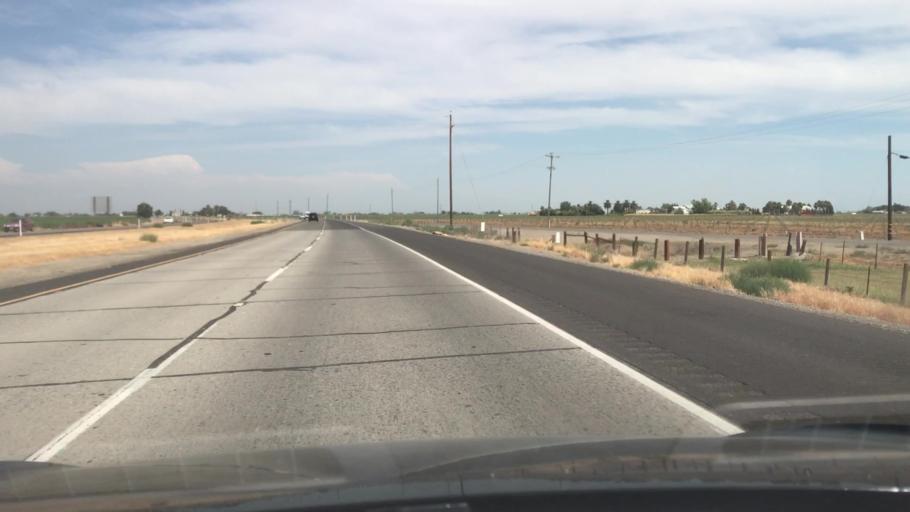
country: US
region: California
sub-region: Merced County
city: Dos Palos
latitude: 37.0482
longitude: -120.6250
